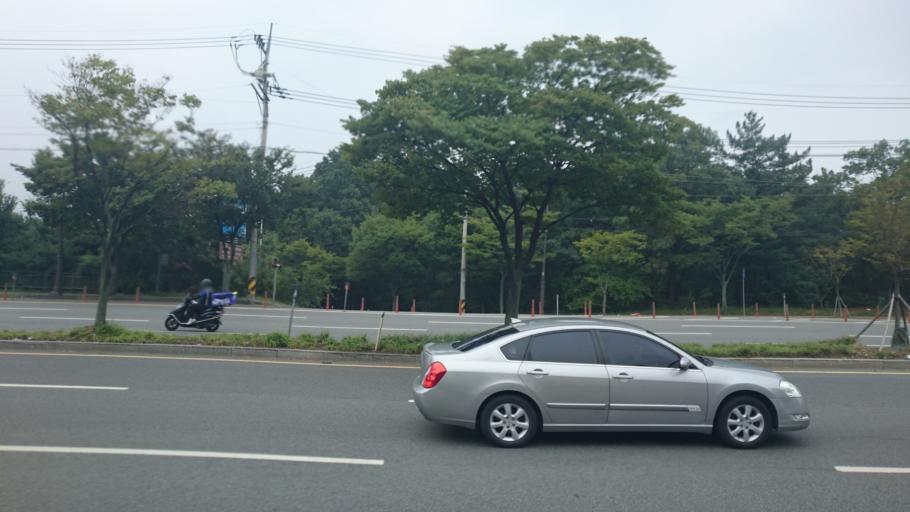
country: KR
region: Daegu
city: Daegu
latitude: 35.8761
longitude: 128.6552
